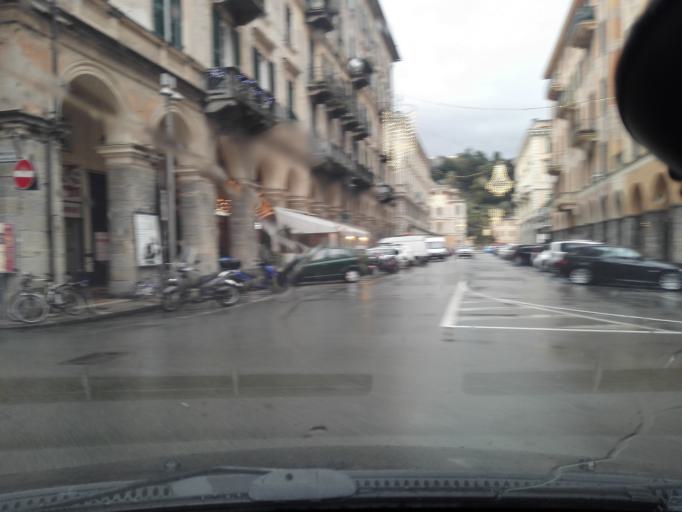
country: IT
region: Liguria
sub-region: Provincia di Genova
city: Chiavari
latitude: 44.3151
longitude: 9.3263
